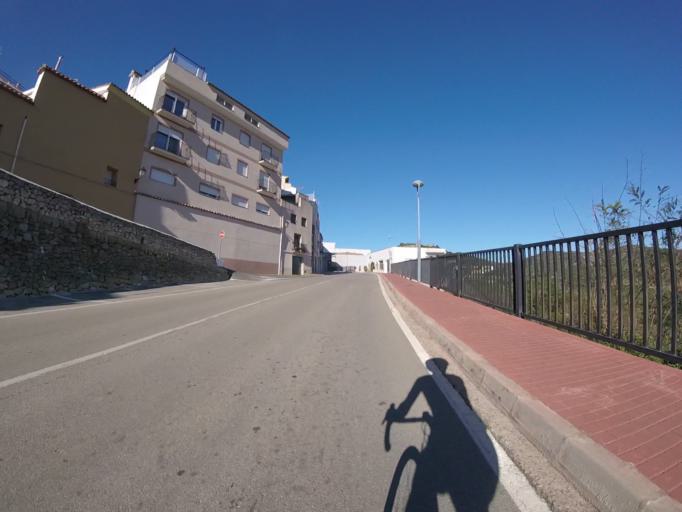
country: ES
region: Valencia
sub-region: Provincia de Castello
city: Cervera del Maestre
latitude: 40.4548
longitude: 0.2793
